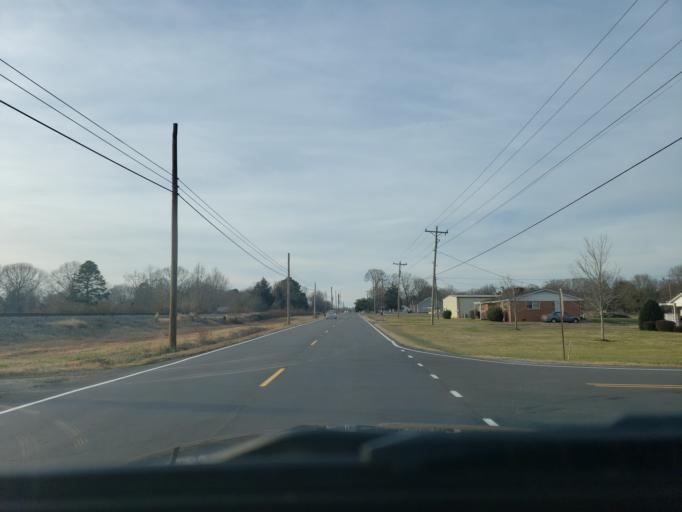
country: US
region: North Carolina
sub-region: Cleveland County
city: Boiling Springs
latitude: 35.3154
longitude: -81.7423
